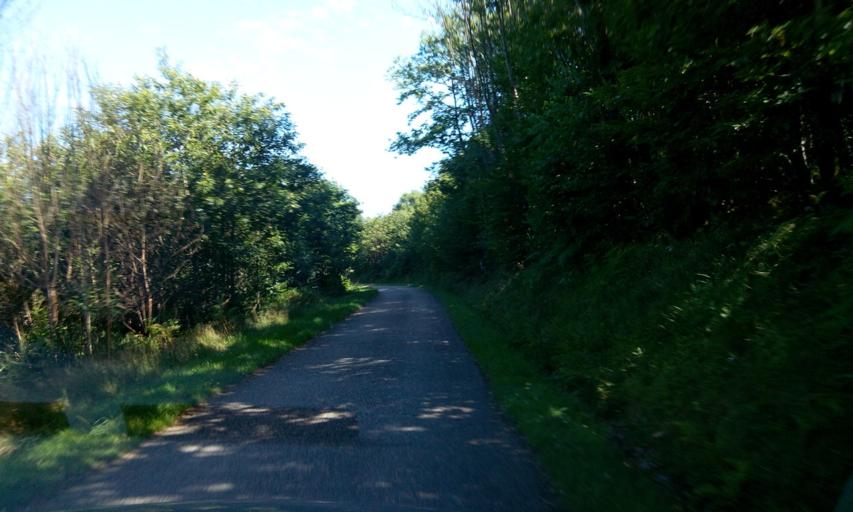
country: FR
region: Limousin
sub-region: Departement de la Correze
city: Beynat
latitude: 45.0842
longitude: 1.7782
